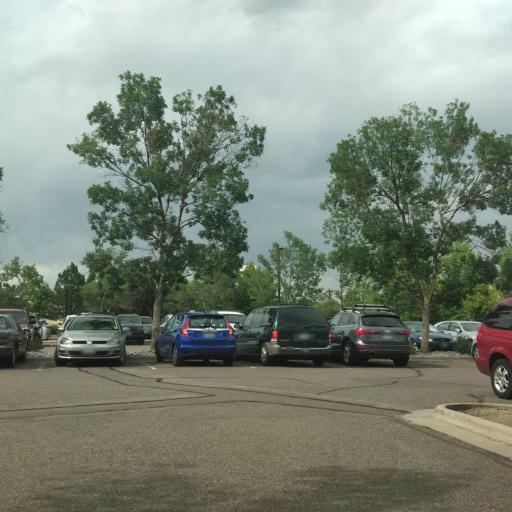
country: US
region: Colorado
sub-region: Jefferson County
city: Lakewood
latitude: 39.7060
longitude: -105.0837
